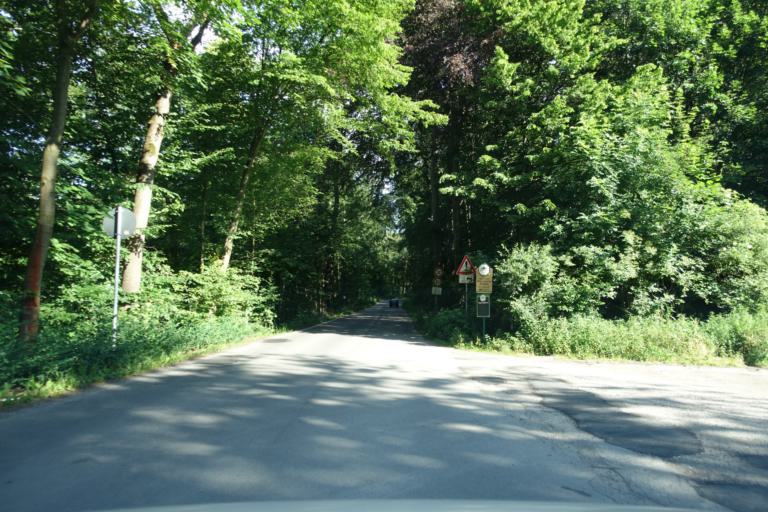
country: DE
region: Saxony
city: Hilbersdorf
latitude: 50.8457
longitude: 12.9629
